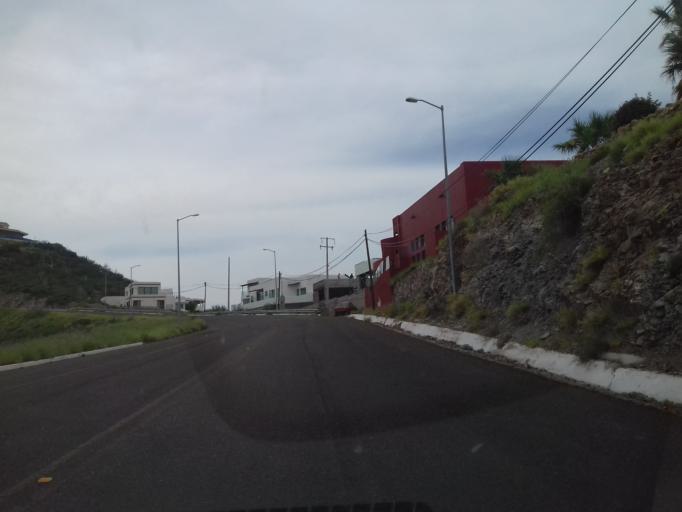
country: MX
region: Sonora
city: Heroica Guaymas
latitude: 27.9429
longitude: -111.0931
